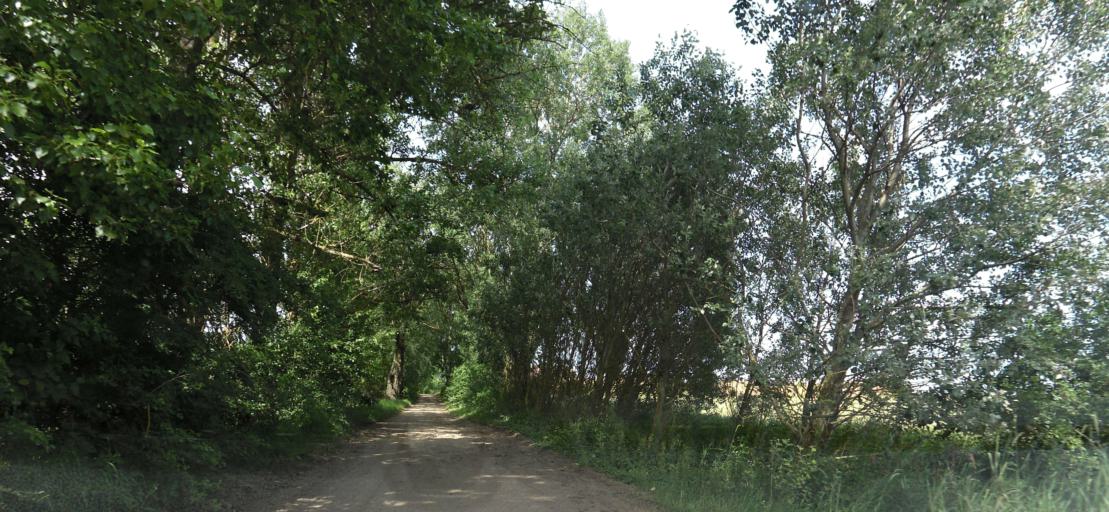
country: LT
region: Panevezys
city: Pasvalys
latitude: 55.9146
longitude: 24.2929
